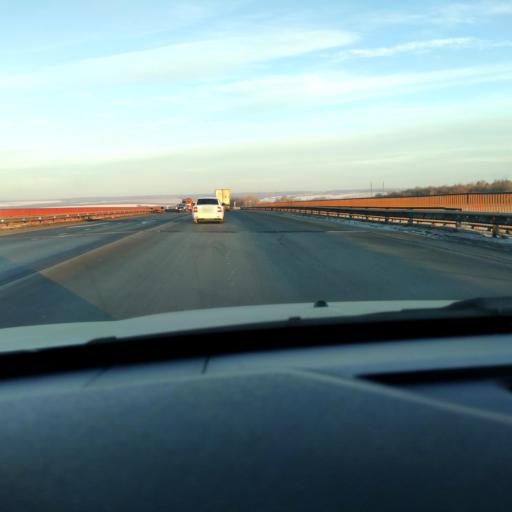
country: RU
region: Samara
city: Smyshlyayevka
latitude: 53.2603
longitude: 50.4741
